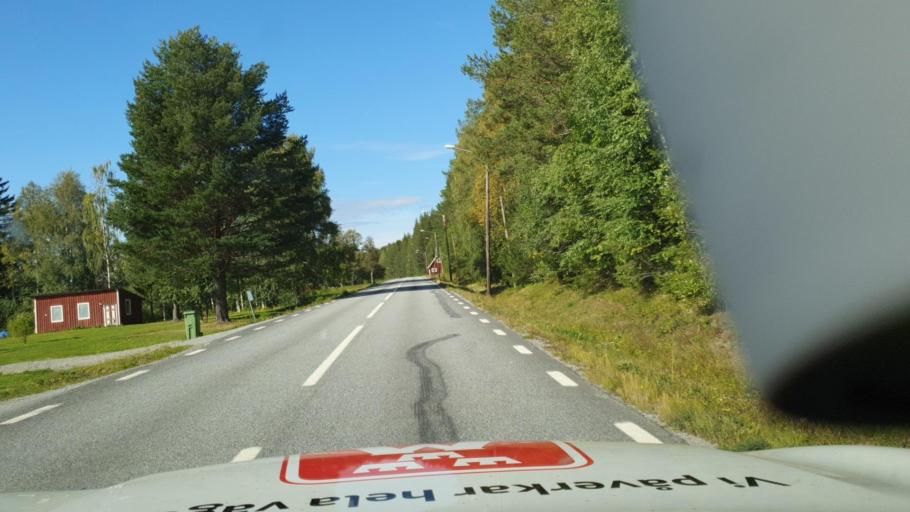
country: SE
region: Vaesterbotten
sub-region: Dorotea Kommun
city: Dorotea
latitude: 64.1152
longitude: 16.2252
